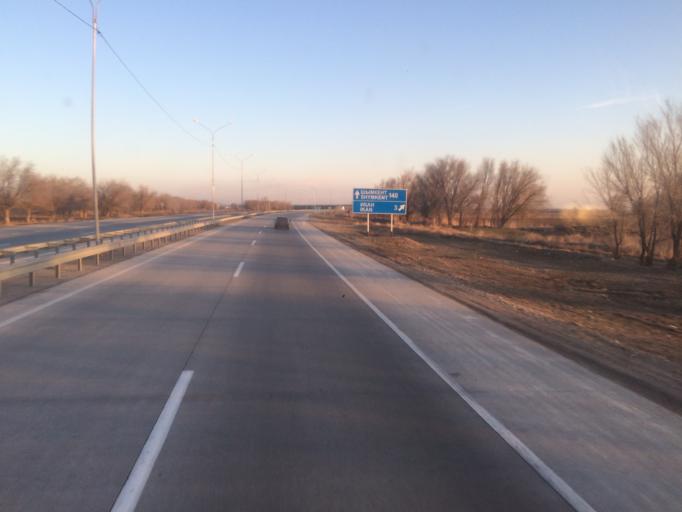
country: KZ
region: Ongtustik Qazaqstan
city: Turkestan
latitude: 43.2157
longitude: 68.4710
